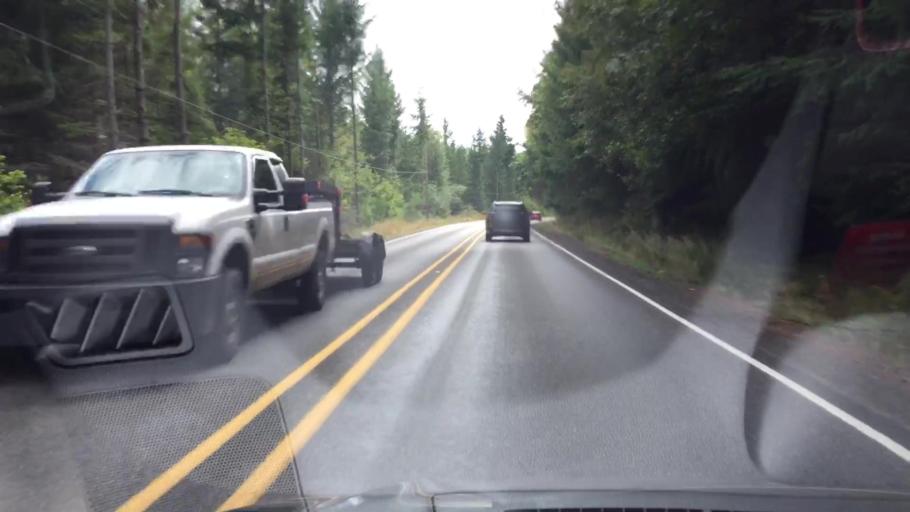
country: US
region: Washington
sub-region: Pierce County
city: Eatonville
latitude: 46.8333
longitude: -122.2514
